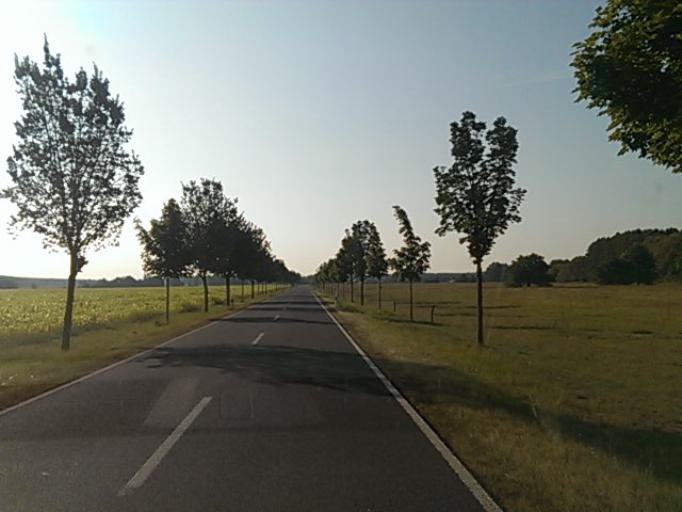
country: DE
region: Brandenburg
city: Trebbin
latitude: 52.2239
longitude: 13.1394
